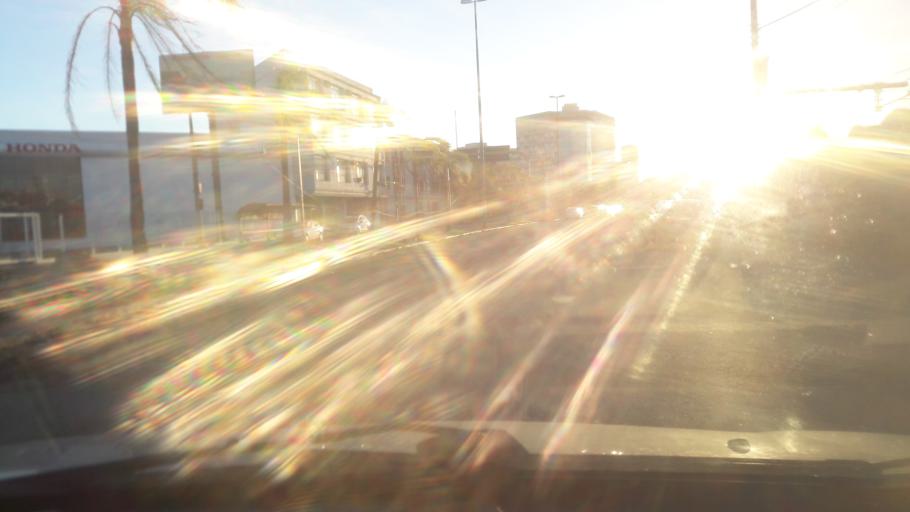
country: BR
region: Rio Grande do Sul
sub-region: Porto Alegre
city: Porto Alegre
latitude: -29.9964
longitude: -51.1902
